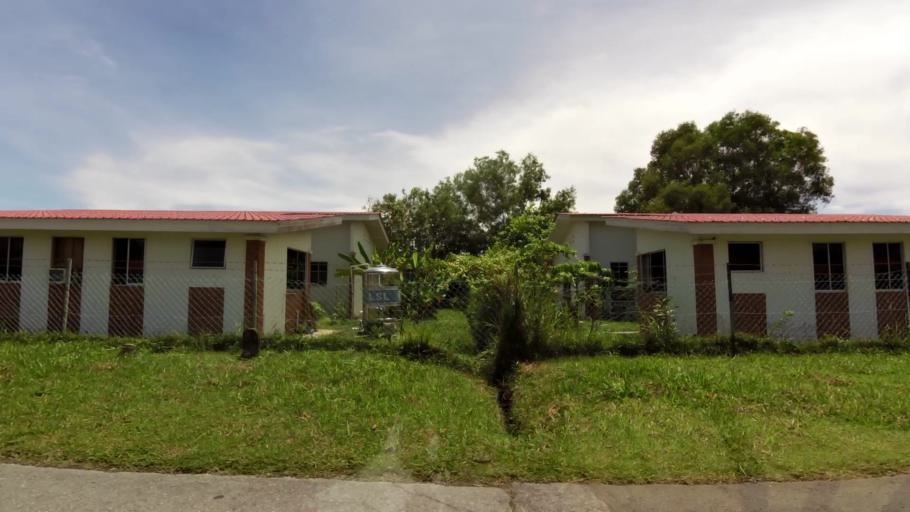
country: BN
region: Belait
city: Kuala Belait
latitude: 4.5934
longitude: 114.2420
